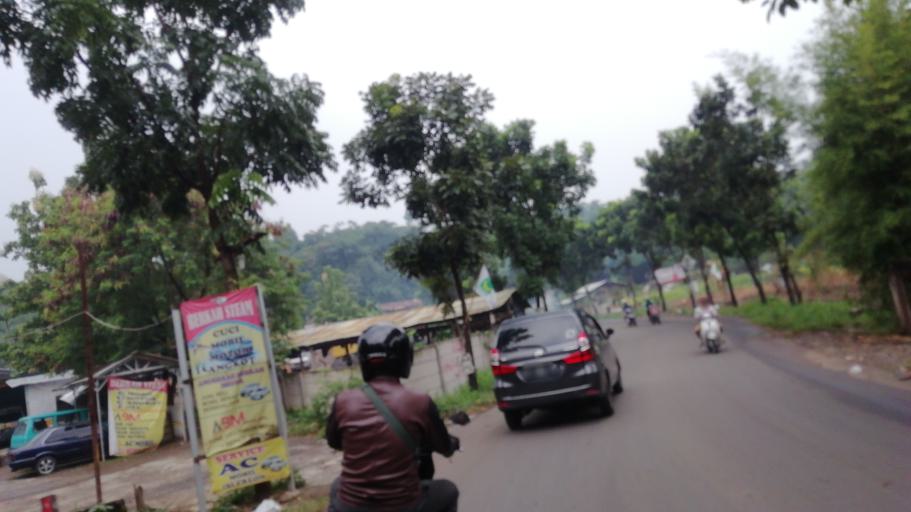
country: ID
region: West Java
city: Bogor
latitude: -6.5310
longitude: 106.8059
